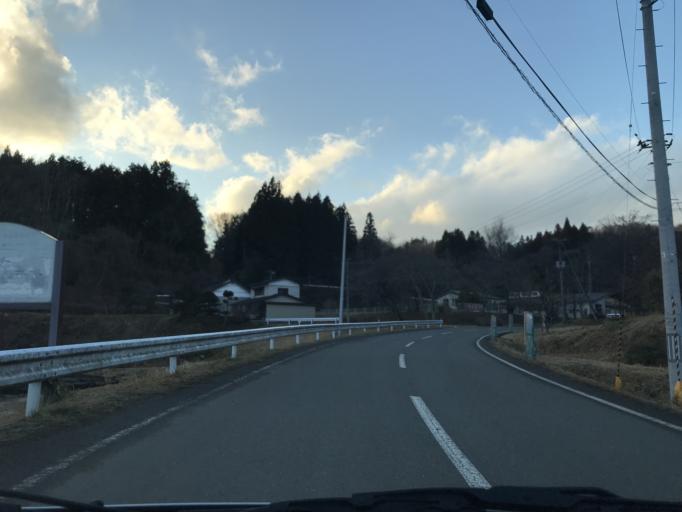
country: JP
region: Iwate
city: Ichinoseki
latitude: 38.9604
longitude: 141.0981
